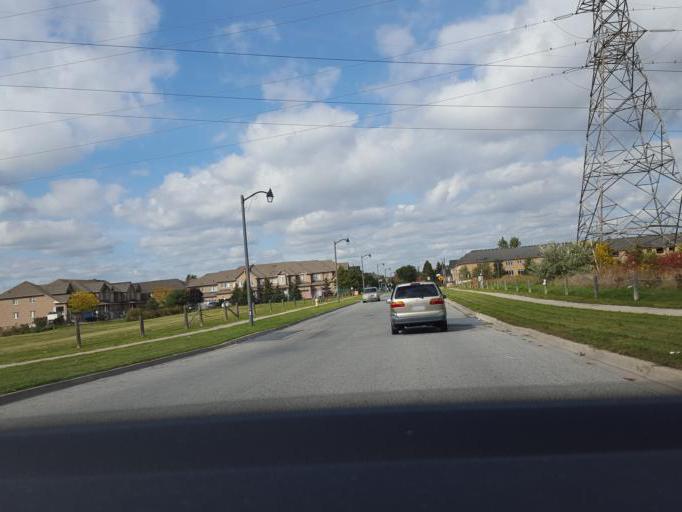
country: CA
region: Ontario
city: Markham
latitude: 43.8286
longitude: -79.2228
